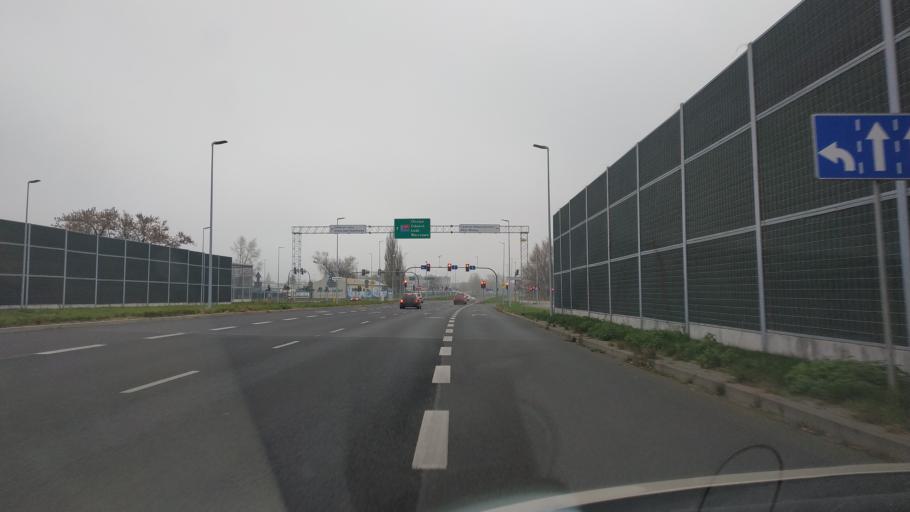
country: PL
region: Kujawsko-Pomorskie
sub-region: Torun
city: Torun
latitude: 53.0298
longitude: 18.6208
